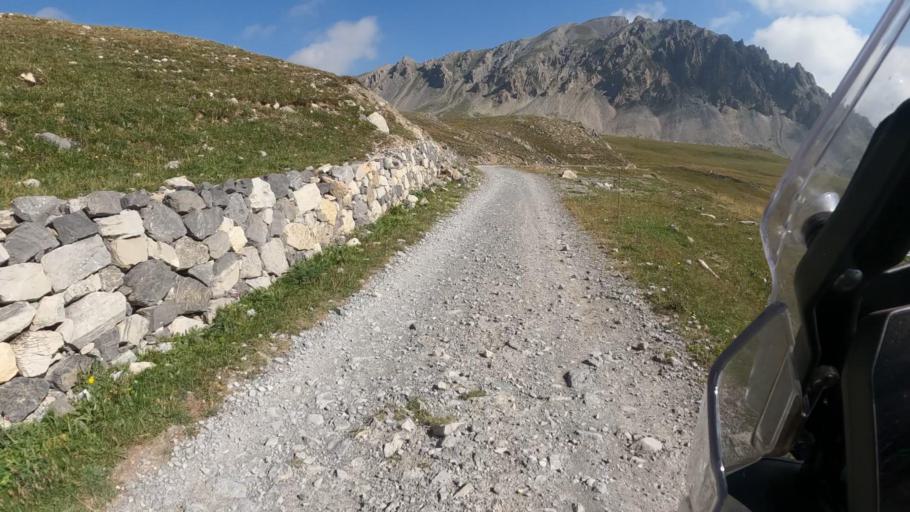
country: IT
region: Piedmont
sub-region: Provincia di Cuneo
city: Bersezio
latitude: 44.4029
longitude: 7.0158
